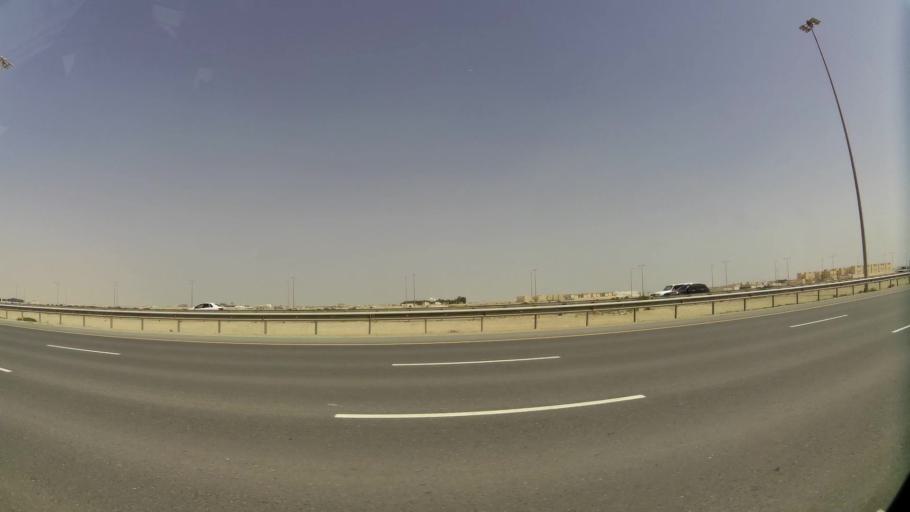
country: QA
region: Baladiyat Umm Salal
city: Umm Salal Muhammad
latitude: 25.4203
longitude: 51.4195
